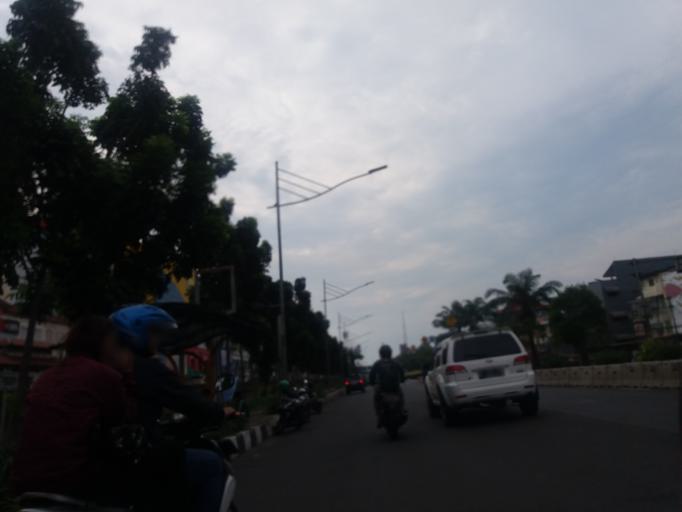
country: ID
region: Jakarta Raya
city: Jakarta
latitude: -6.1407
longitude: 106.8331
